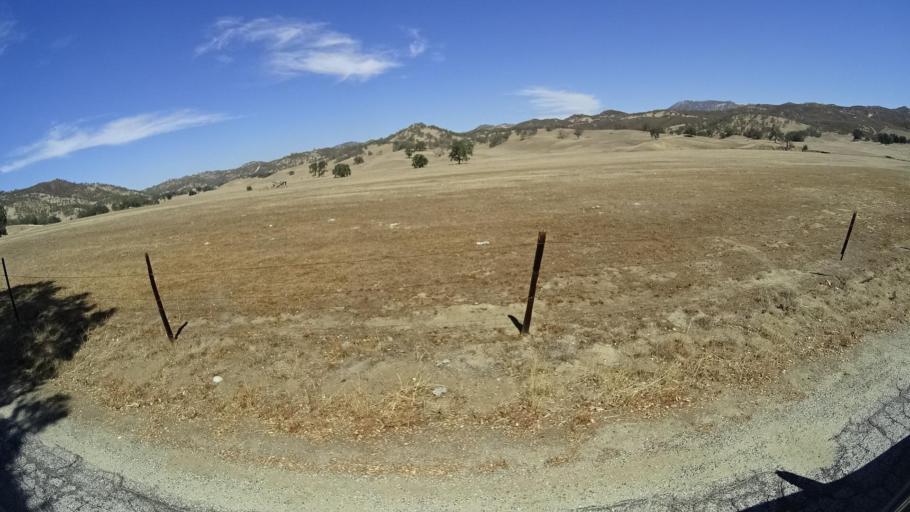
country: US
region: California
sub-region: San Luis Obispo County
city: San Miguel
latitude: 36.0328
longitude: -120.6616
